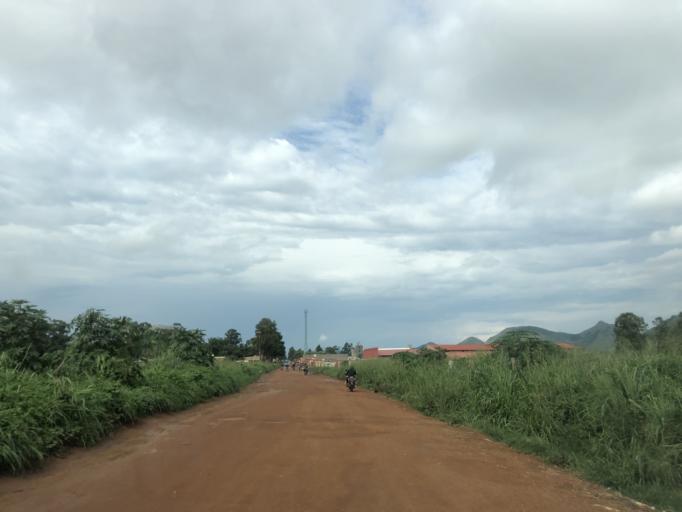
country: AO
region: Cuanza Sul
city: Uacu Cungo
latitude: -11.3477
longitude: 15.1044
